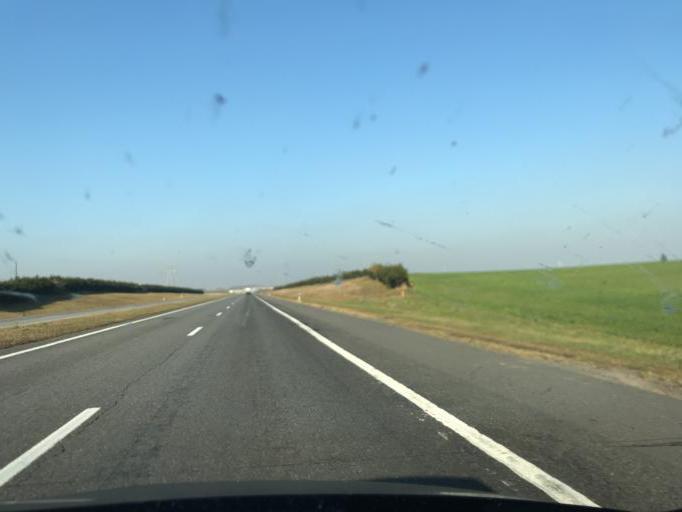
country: BY
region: Grodnenskaya
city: Mir
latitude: 53.4339
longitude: 26.5866
